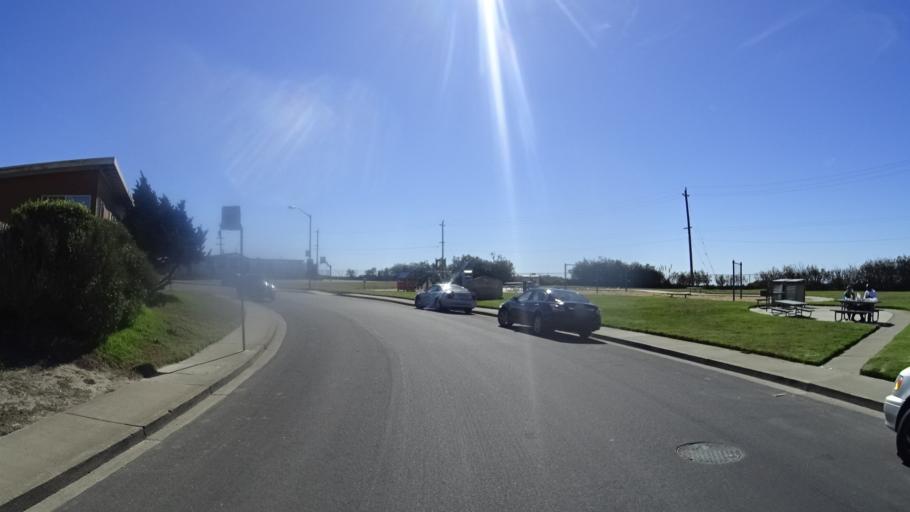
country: US
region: California
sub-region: San Mateo County
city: Broadmoor
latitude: 37.6802
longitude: -122.4936
